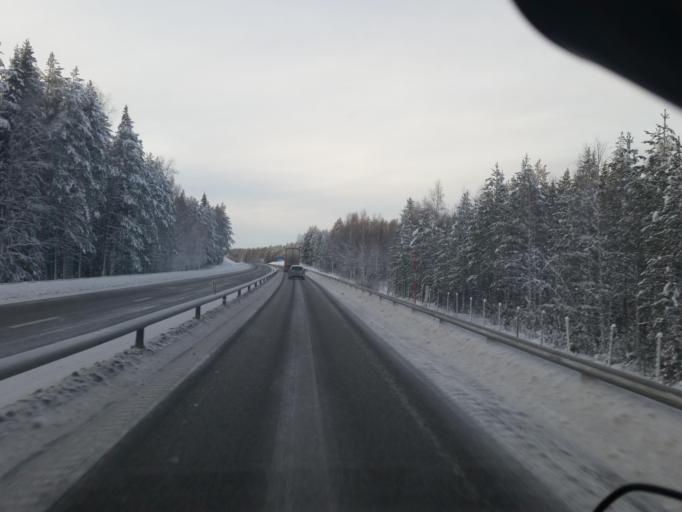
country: SE
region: Norrbotten
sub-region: Pitea Kommun
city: Rosvik
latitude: 65.4302
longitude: 21.5869
